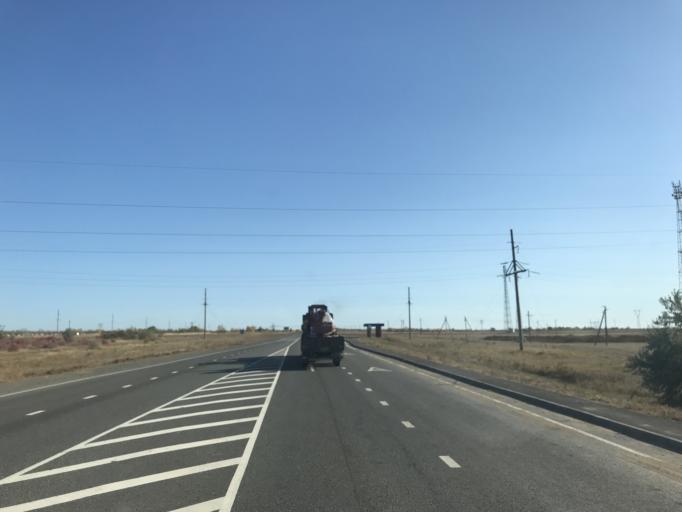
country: KZ
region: Pavlodar
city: Koktobe
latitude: 51.9250
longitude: 77.3357
